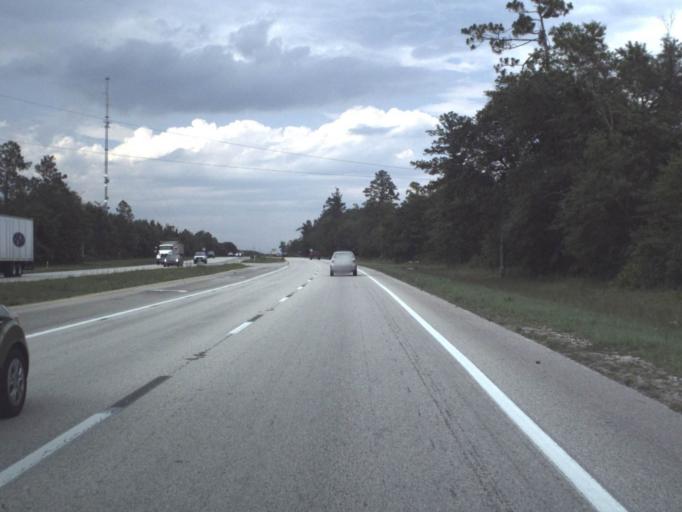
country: US
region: Florida
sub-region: Bradford County
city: Starke
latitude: 30.1032
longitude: -82.0523
